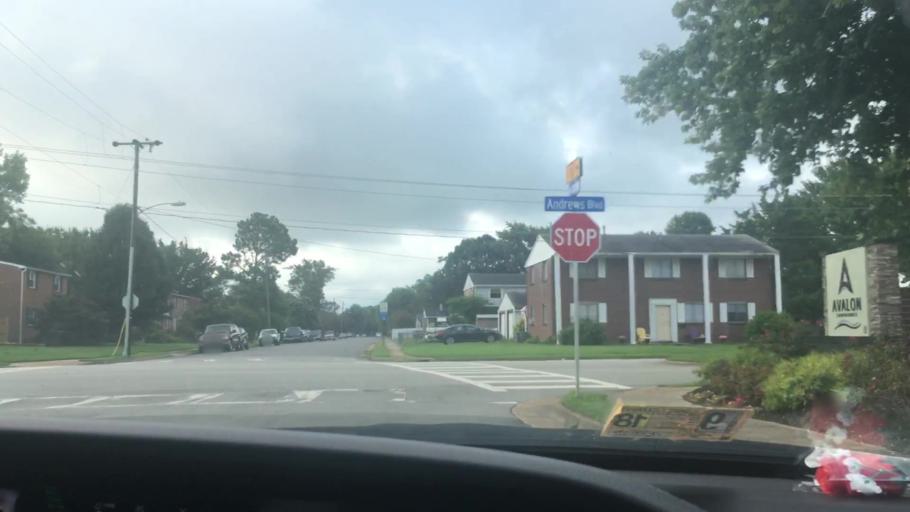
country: US
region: Virginia
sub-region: City of Hampton
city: East Hampton
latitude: 37.0495
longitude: -76.3063
